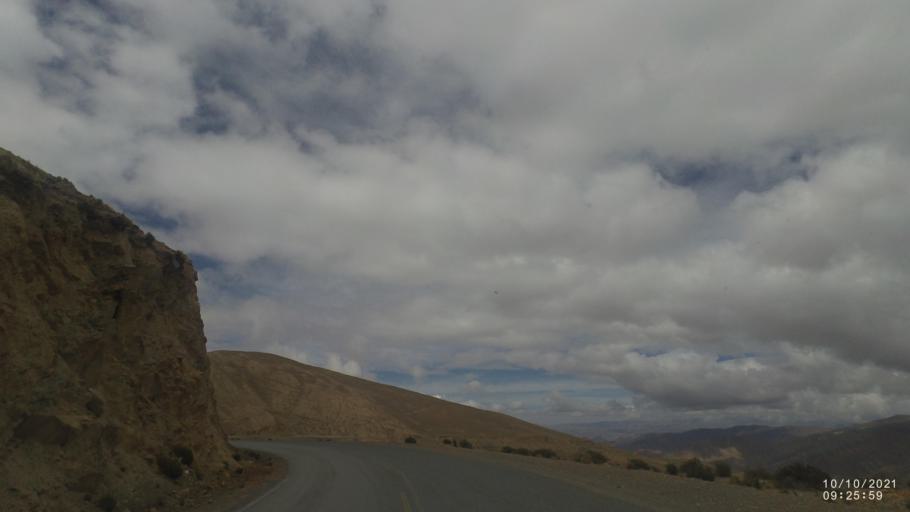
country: BO
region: La Paz
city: Quime
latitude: -17.0933
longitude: -67.3191
